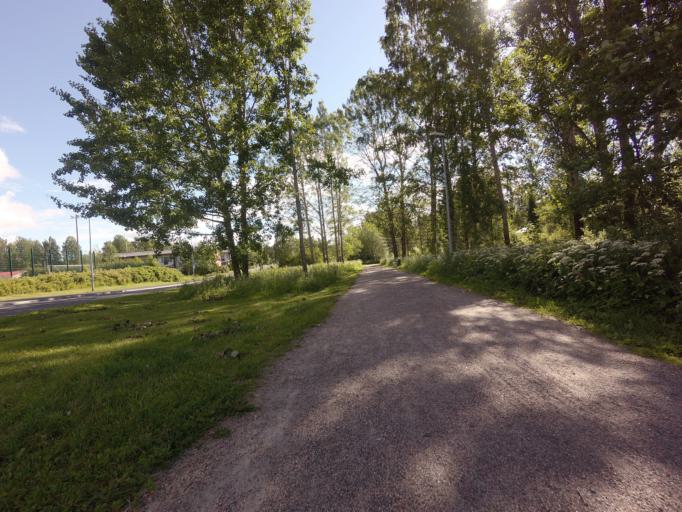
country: FI
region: Uusimaa
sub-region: Helsinki
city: Espoo
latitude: 60.1759
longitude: 24.6535
